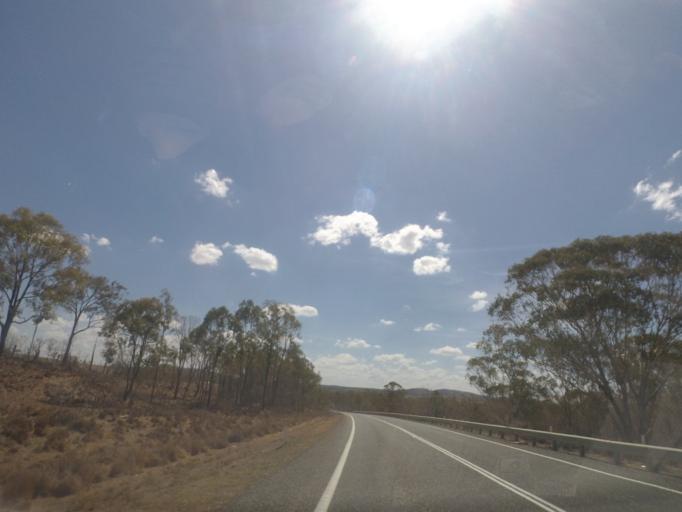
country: AU
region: Queensland
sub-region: Southern Downs
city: Warwick
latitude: -28.2053
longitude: 151.5731
